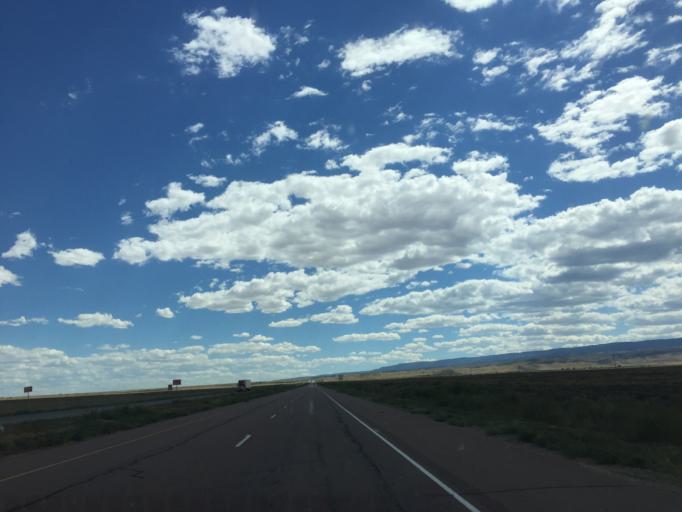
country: US
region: New Mexico
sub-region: McKinley County
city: Navajo
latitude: 36.2214
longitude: -108.7093
